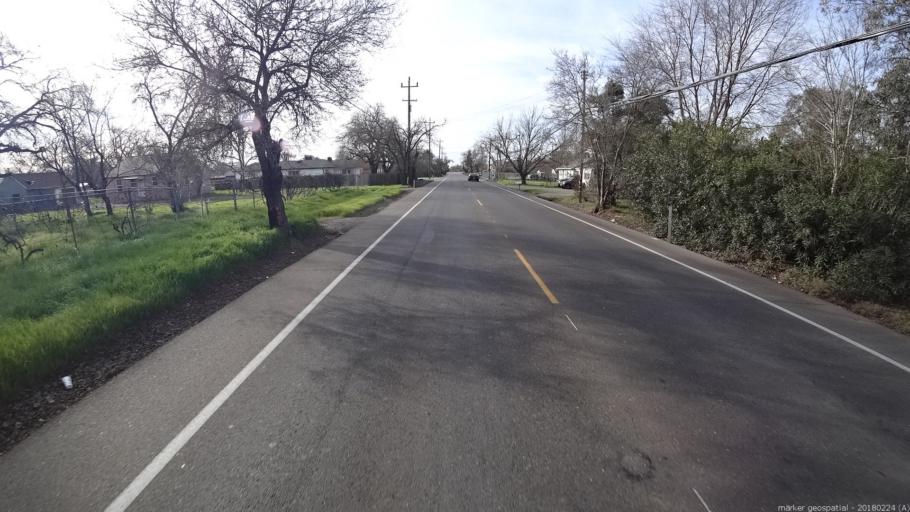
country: US
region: California
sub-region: Sacramento County
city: Rio Linda
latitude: 38.6780
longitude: -121.4569
